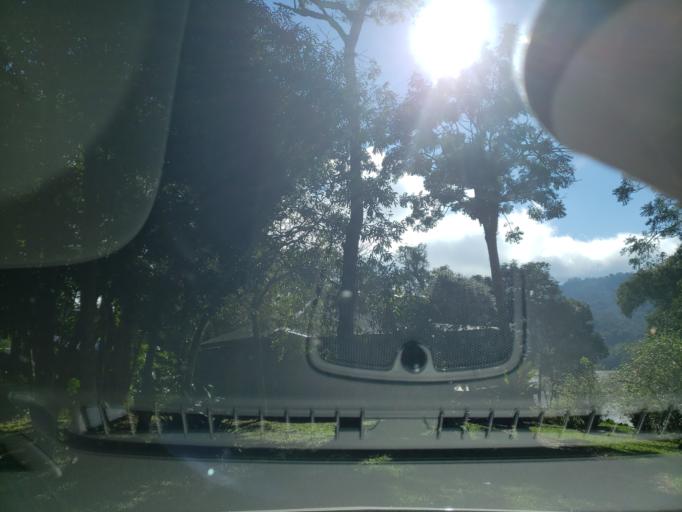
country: AR
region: Misiones
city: El Soberbio
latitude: -27.2270
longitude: -54.0172
